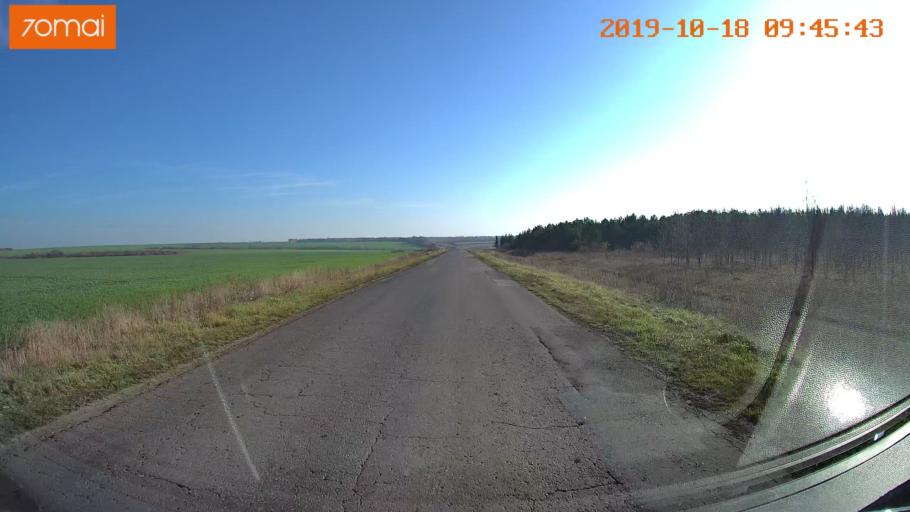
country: RU
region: Tula
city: Kazachka
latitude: 53.3125
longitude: 38.1964
